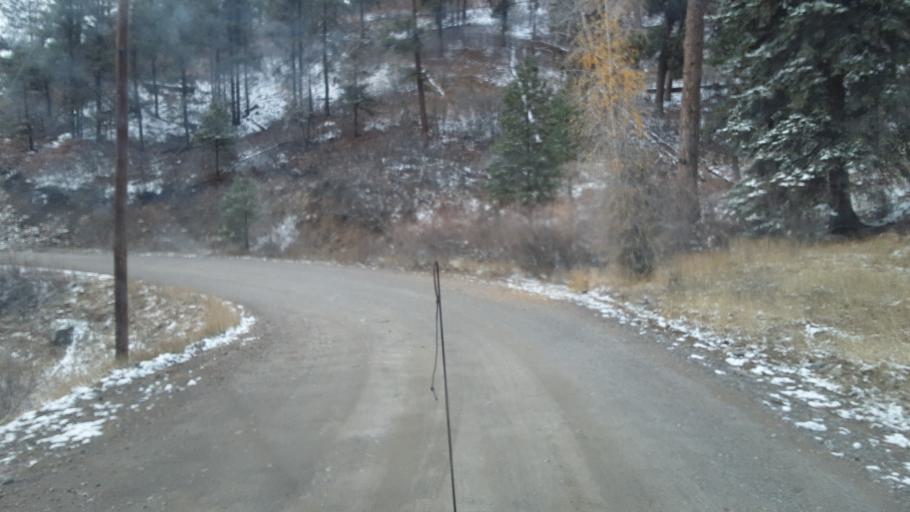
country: US
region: Colorado
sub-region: La Plata County
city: Bayfield
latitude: 37.4086
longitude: -107.5304
